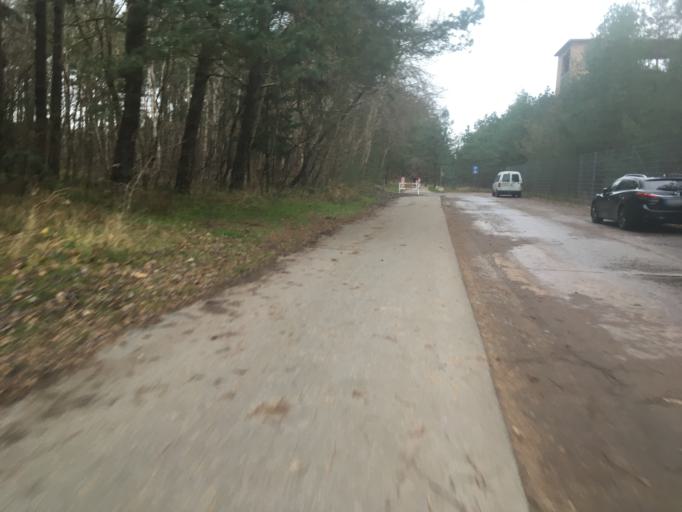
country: DE
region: Mecklenburg-Vorpommern
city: Sagard
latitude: 54.4573
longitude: 13.5673
